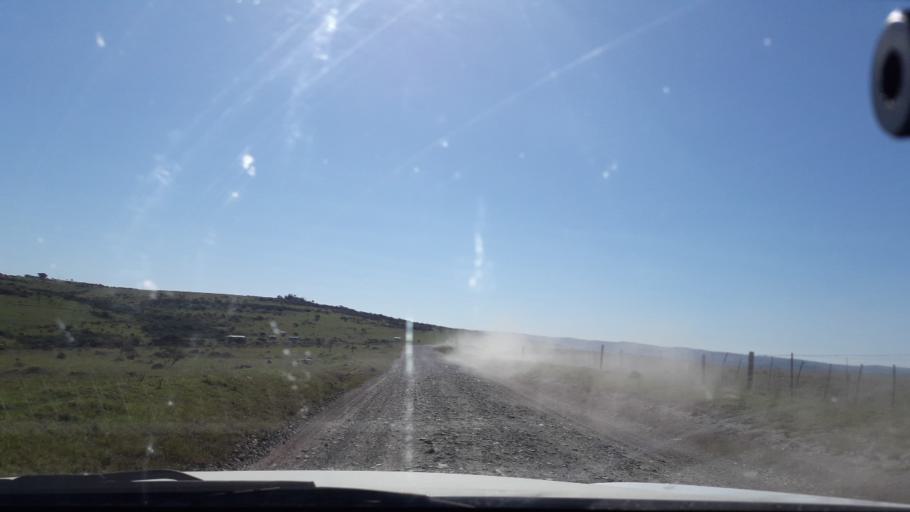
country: ZA
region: Eastern Cape
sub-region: Buffalo City Metropolitan Municipality
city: East London
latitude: -32.7957
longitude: 27.9512
